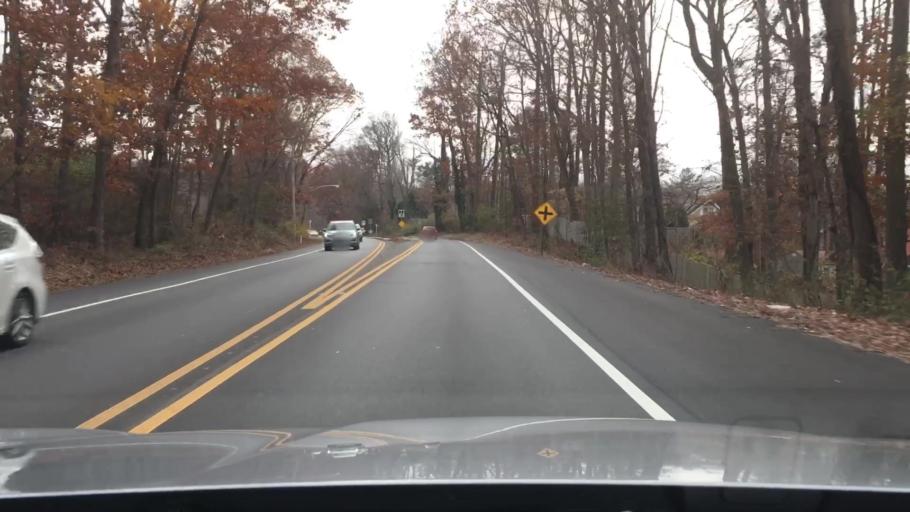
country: US
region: Maryland
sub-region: Prince George's County
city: Bowie
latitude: 38.9636
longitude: -76.7522
